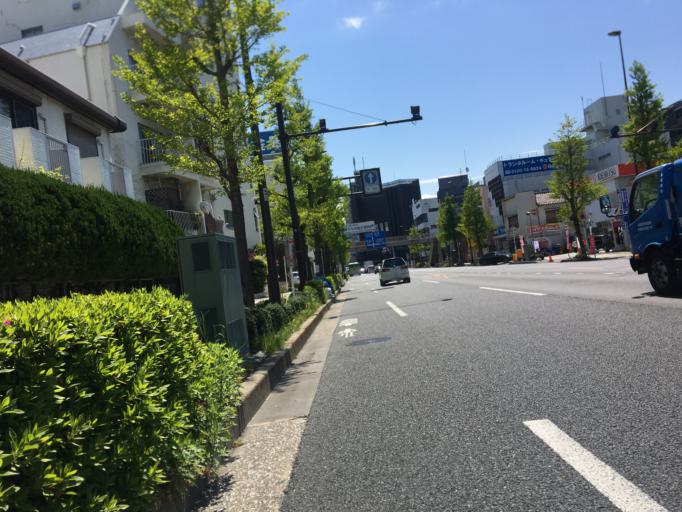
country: JP
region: Saitama
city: Shimotoda
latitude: 35.7865
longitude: 139.6856
